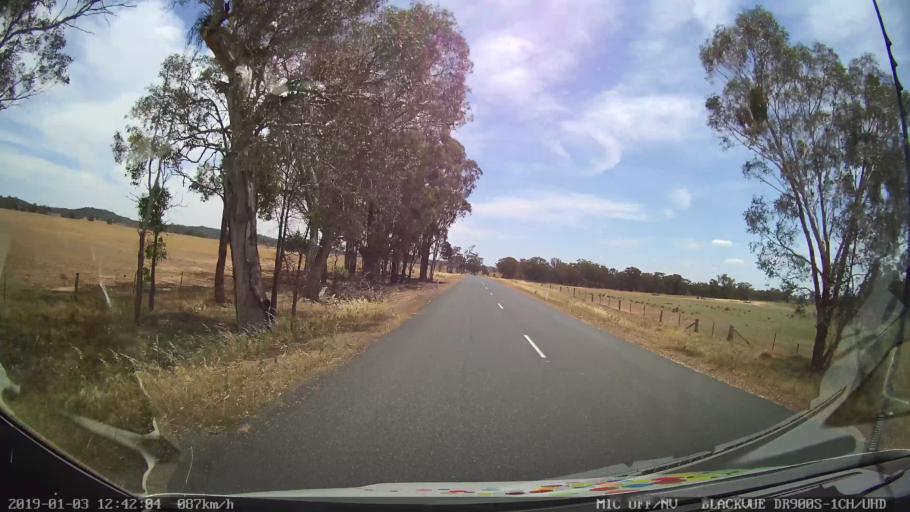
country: AU
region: New South Wales
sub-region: Weddin
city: Grenfell
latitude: -33.7915
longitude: 148.2137
